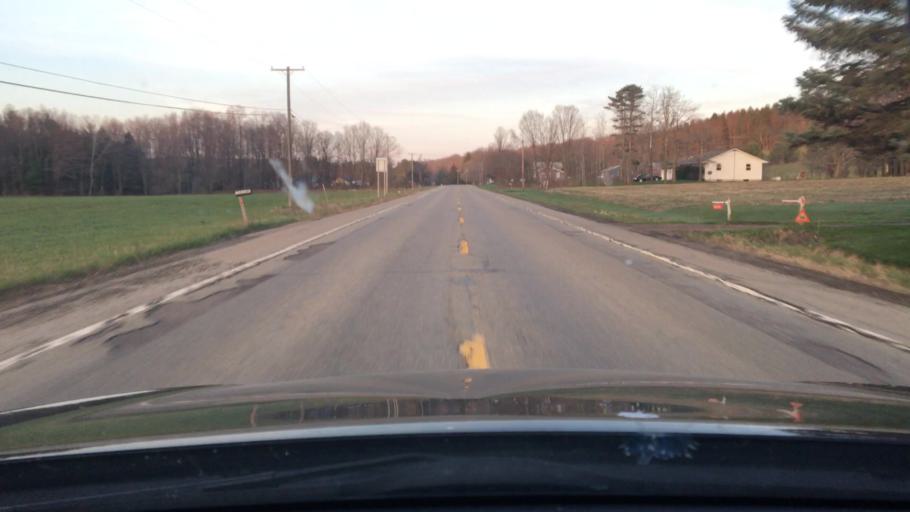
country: US
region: New York
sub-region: Cattaraugus County
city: Randolph
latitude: 42.1794
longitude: -78.9259
